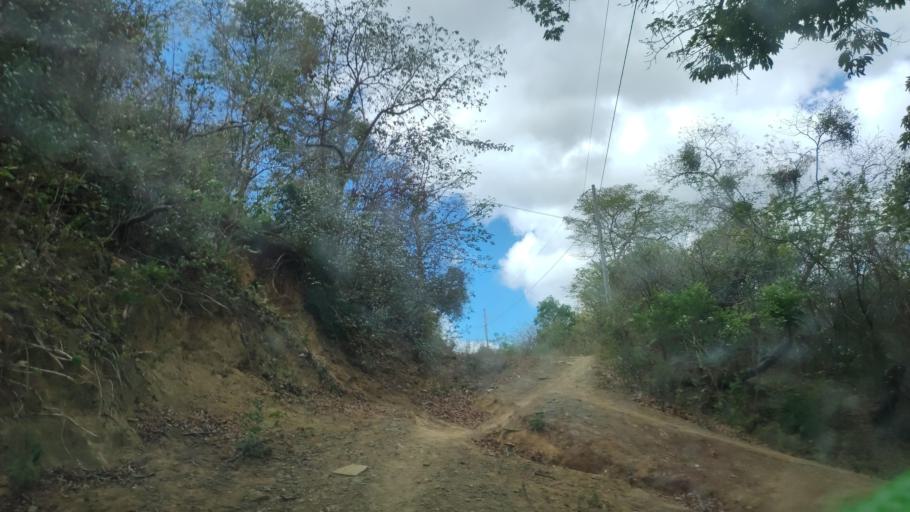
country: NI
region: Carazo
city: Santa Teresa
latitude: 11.6336
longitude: -86.2252
